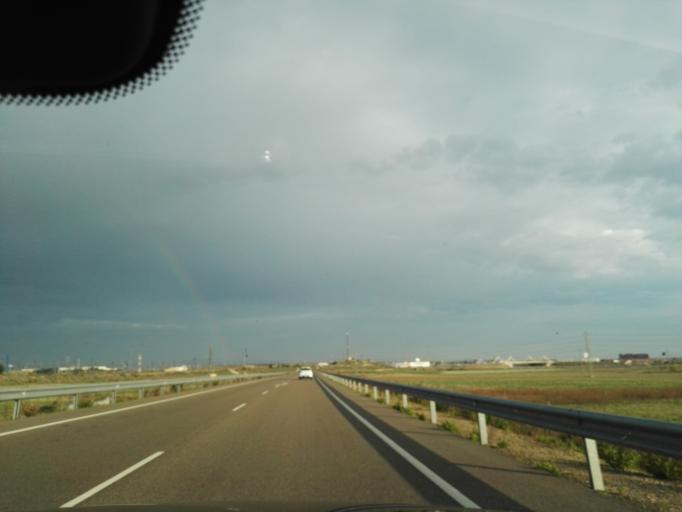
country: ES
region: Aragon
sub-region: Provincia de Zaragoza
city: Montecanal
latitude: 41.6232
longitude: -0.9826
